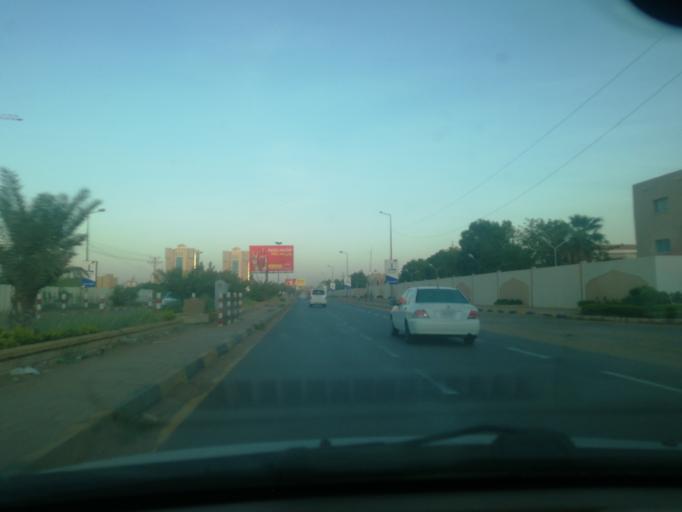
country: SD
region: Khartoum
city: Khartoum
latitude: 15.6207
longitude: 32.5687
